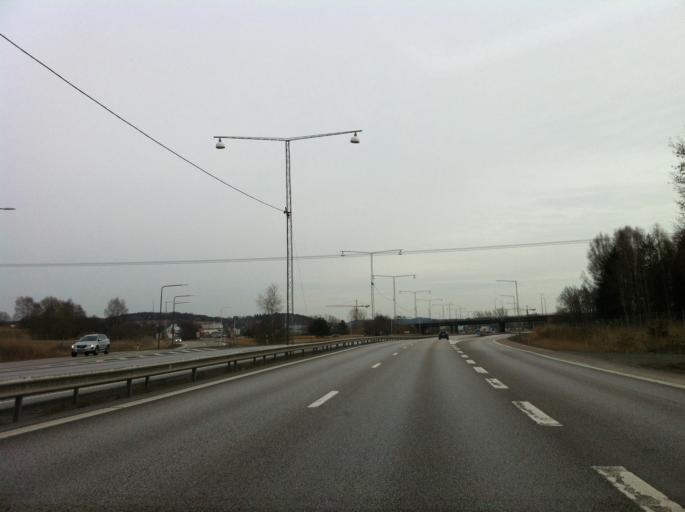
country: SE
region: Vaestra Goetaland
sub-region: Kungalvs Kommun
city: Kode
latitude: 57.9128
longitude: 11.8915
